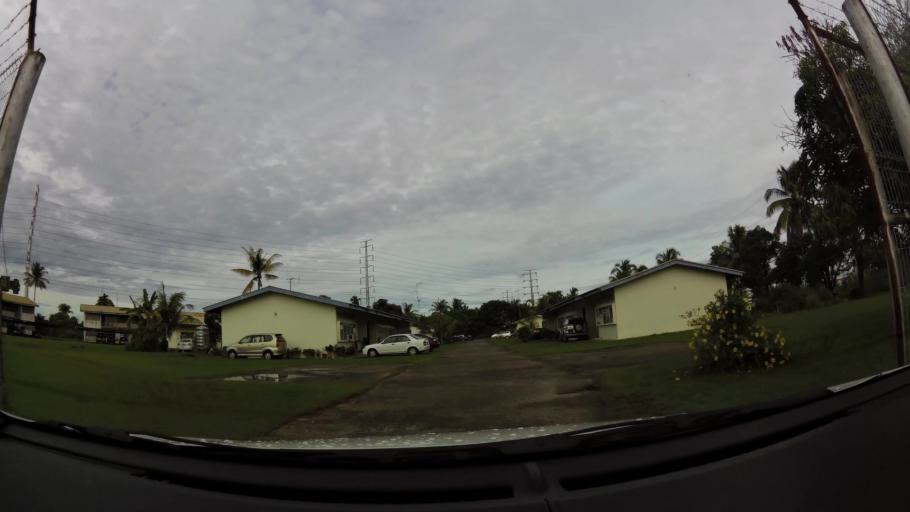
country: BN
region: Belait
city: Seria
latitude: 4.6160
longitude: 114.3461
